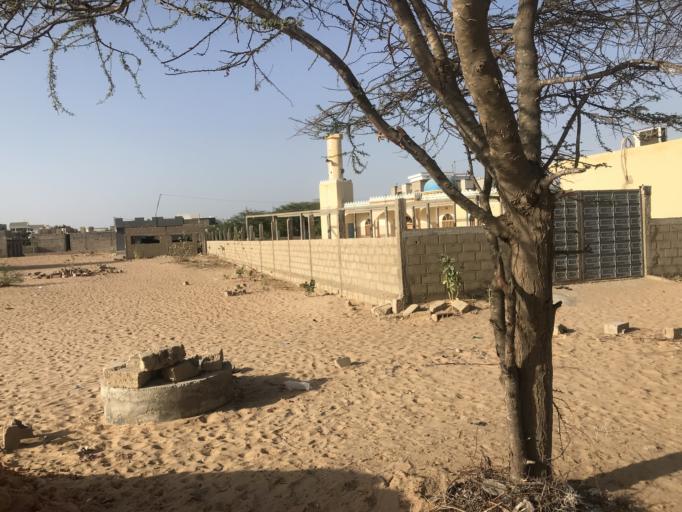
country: SN
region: Saint-Louis
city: Saint-Louis
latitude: 16.0365
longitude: -16.4421
